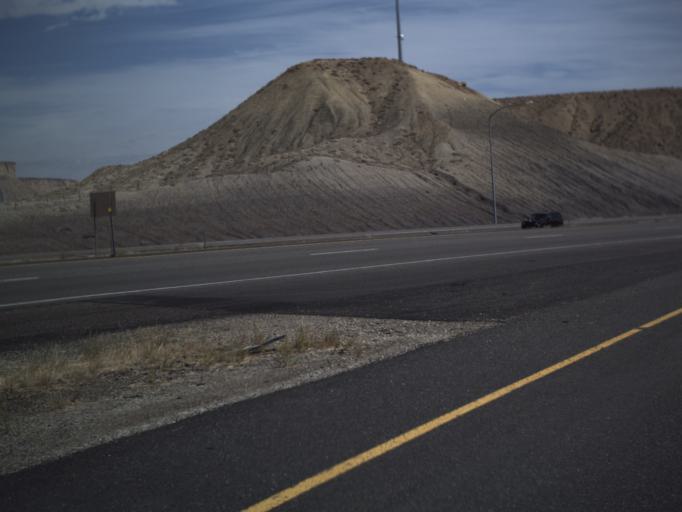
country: US
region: Utah
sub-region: Grand County
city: Moab
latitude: 38.9617
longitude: -109.7188
